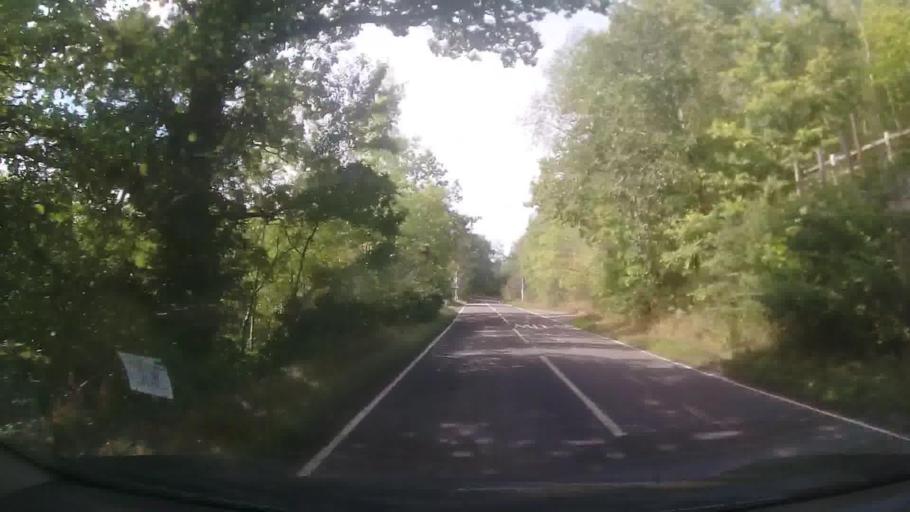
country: GB
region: England
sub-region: Shropshire
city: Lydham
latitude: 52.5327
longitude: -2.9988
